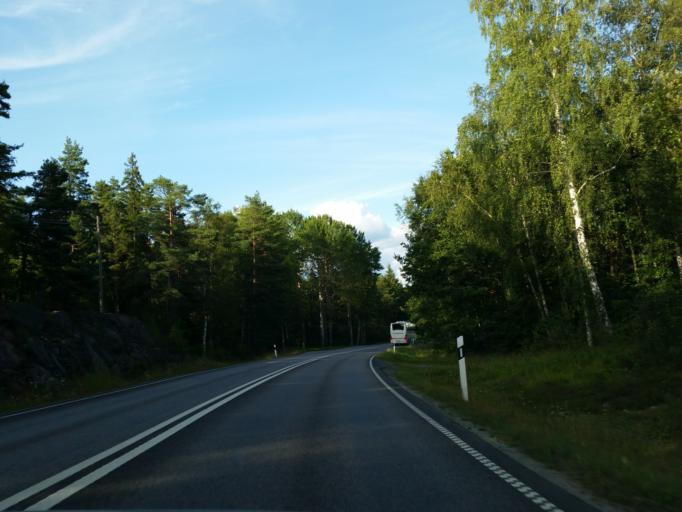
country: SE
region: Stockholm
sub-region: Sodertalje Kommun
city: Molnbo
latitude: 59.0571
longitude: 17.4658
